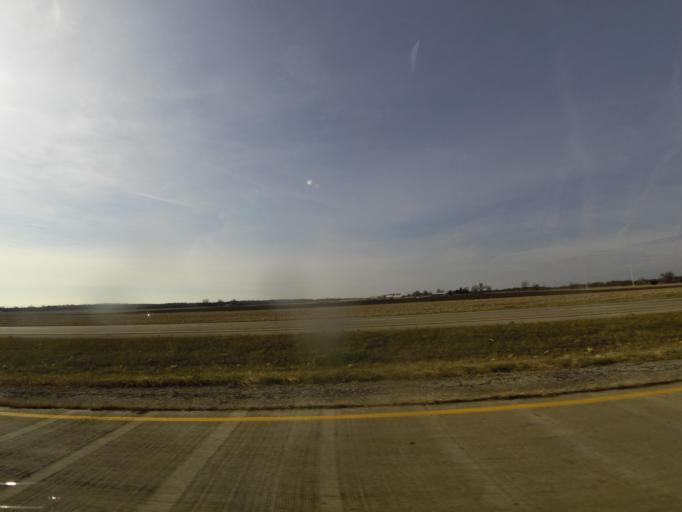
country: US
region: Illinois
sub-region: De Witt County
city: Clinton
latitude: 40.1447
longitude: -88.9829
